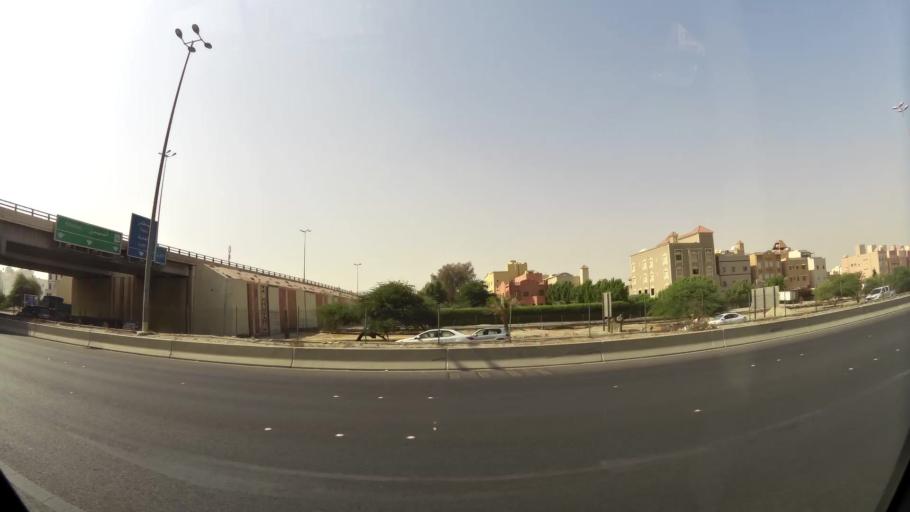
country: KW
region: Al Ahmadi
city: Al Fintas
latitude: 29.1794
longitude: 48.1138
